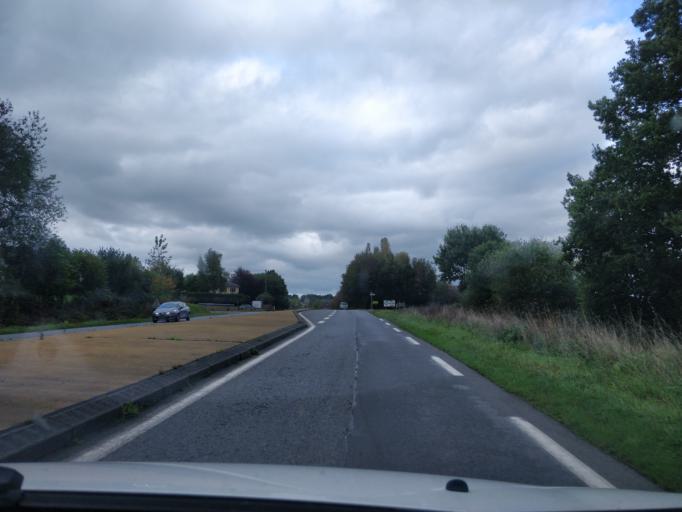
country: FR
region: Lower Normandy
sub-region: Departement de la Manche
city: Villedieu-les-Poeles
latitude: 48.8398
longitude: -1.2012
